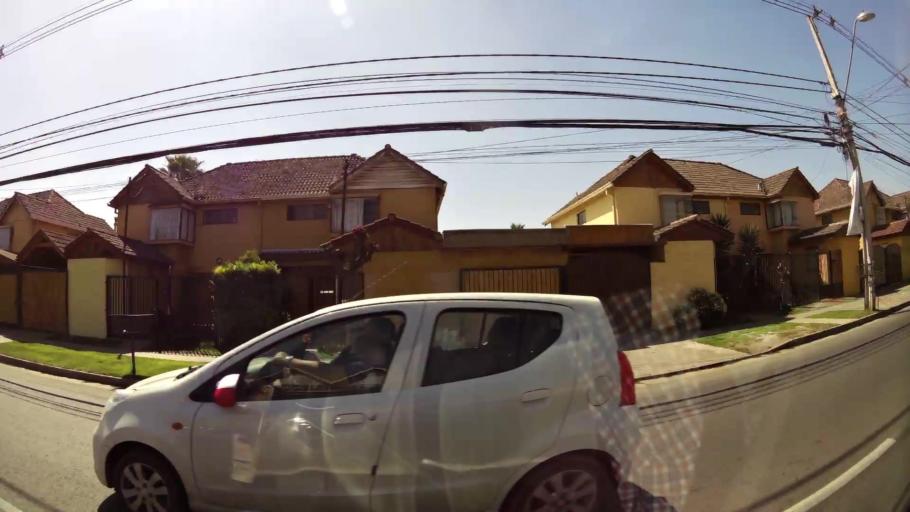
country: CL
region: Santiago Metropolitan
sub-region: Provincia de Santiago
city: Lo Prado
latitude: -33.3533
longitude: -70.7269
